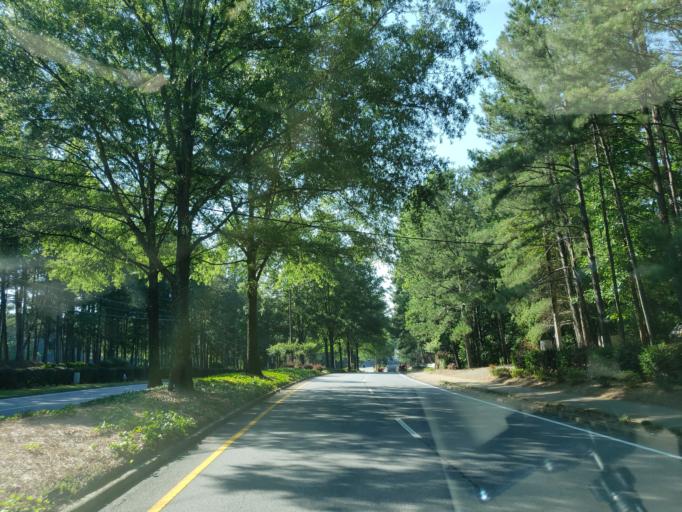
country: US
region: Georgia
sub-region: Cherokee County
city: Woodstock
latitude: 34.1238
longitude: -84.5582
